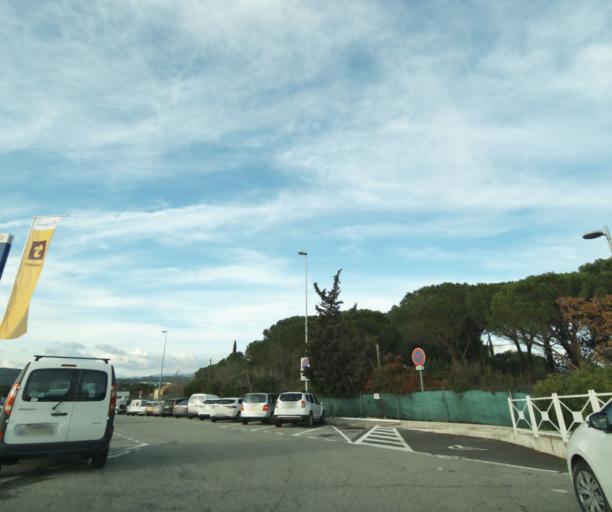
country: FR
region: Provence-Alpes-Cote d'Azur
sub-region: Departement du Var
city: Le Muy
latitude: 43.4613
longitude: 6.5505
